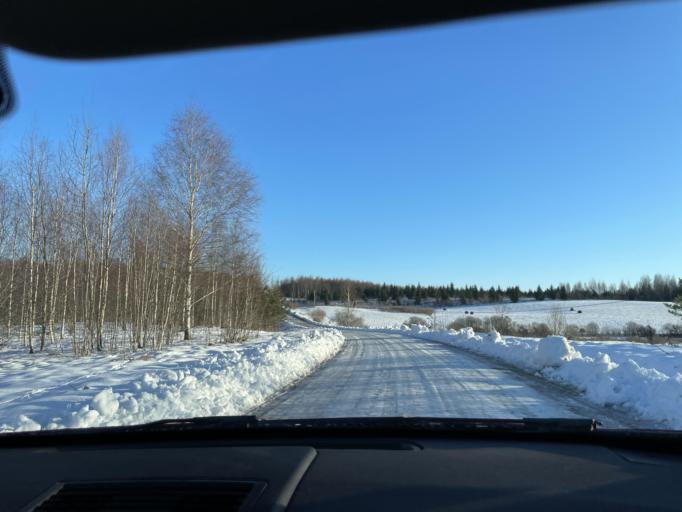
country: LV
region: Ludzas Rajons
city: Ludza
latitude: 56.4601
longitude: 27.6122
